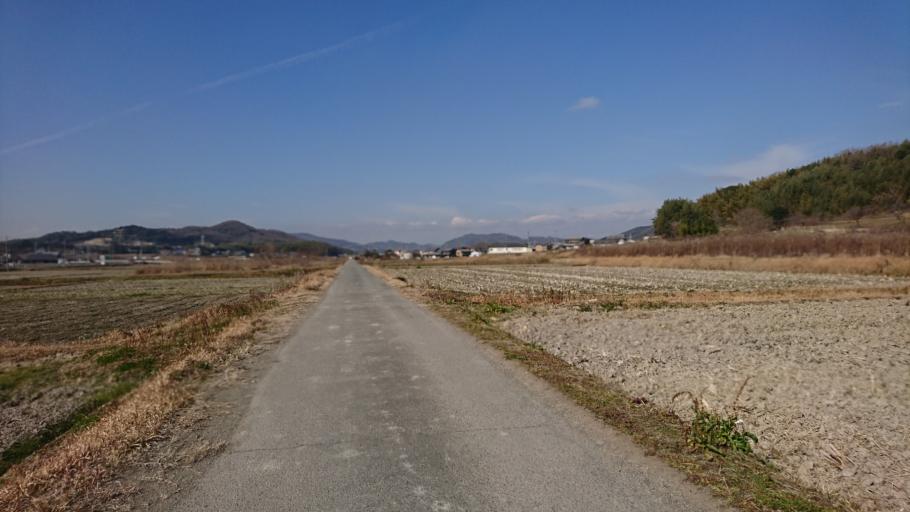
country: JP
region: Hyogo
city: Kakogawacho-honmachi
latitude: 34.8126
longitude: 134.8580
